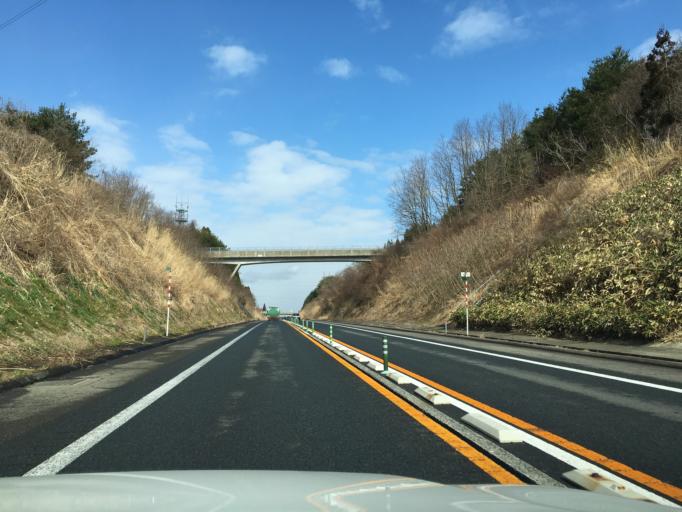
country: JP
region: Akita
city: Akita Shi
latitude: 39.8079
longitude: 140.0944
